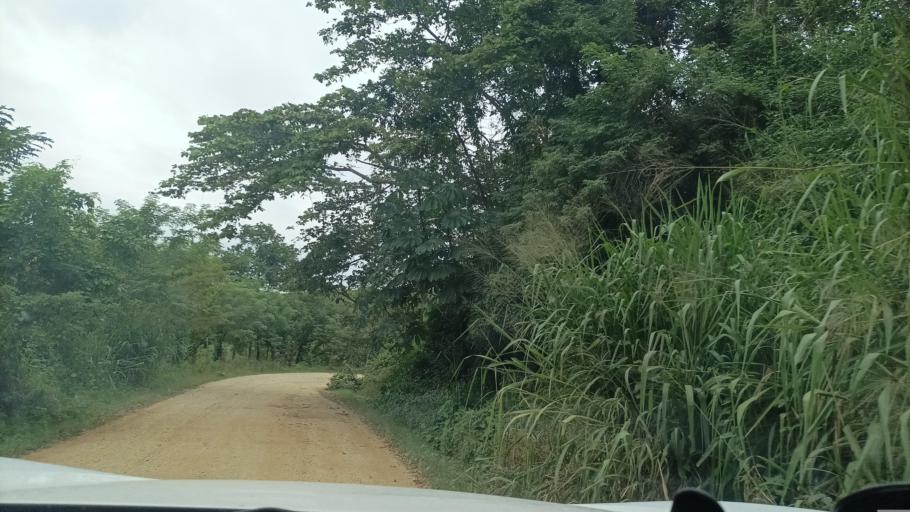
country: MX
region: Veracruz
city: Hidalgotitlan
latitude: 17.6211
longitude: -94.5149
